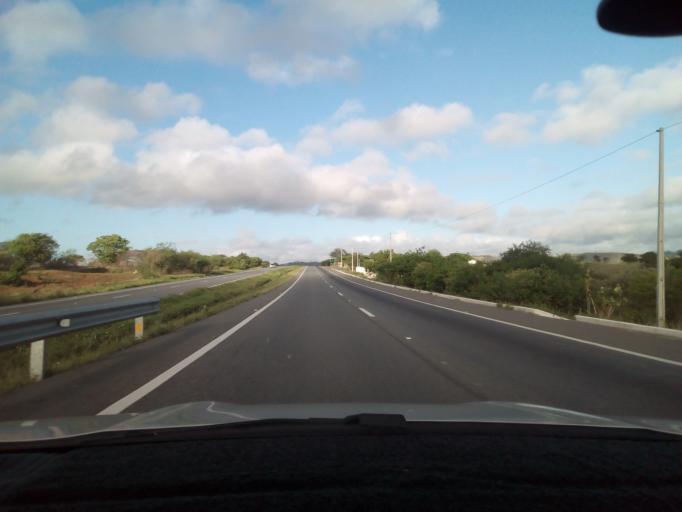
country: BR
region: Paraiba
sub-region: Serra Redonda
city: Alagoa Grande
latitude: -7.2091
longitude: -35.5748
